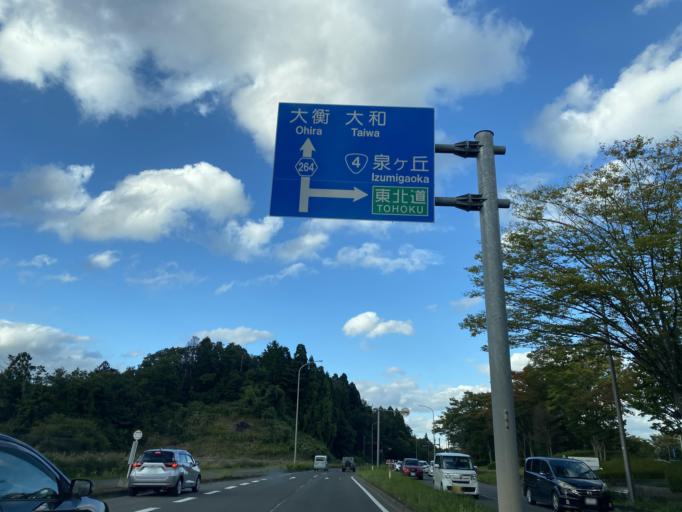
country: JP
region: Miyagi
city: Tomiya
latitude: 38.3539
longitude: 140.8431
